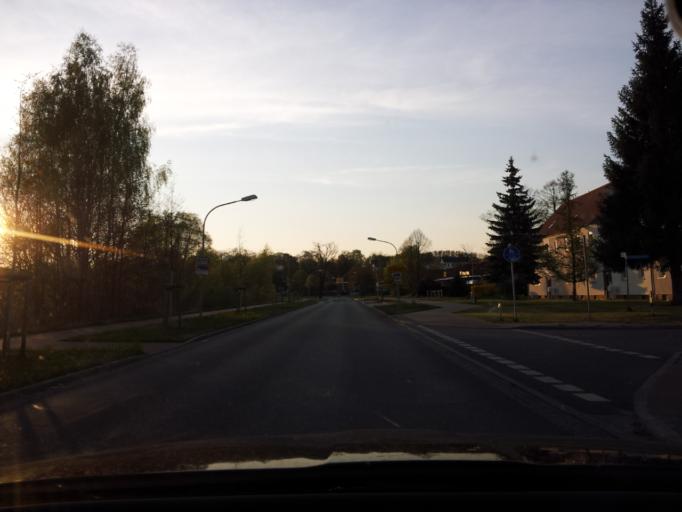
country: DE
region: Brandenburg
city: Juterbog
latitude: 51.9945
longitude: 13.0576
